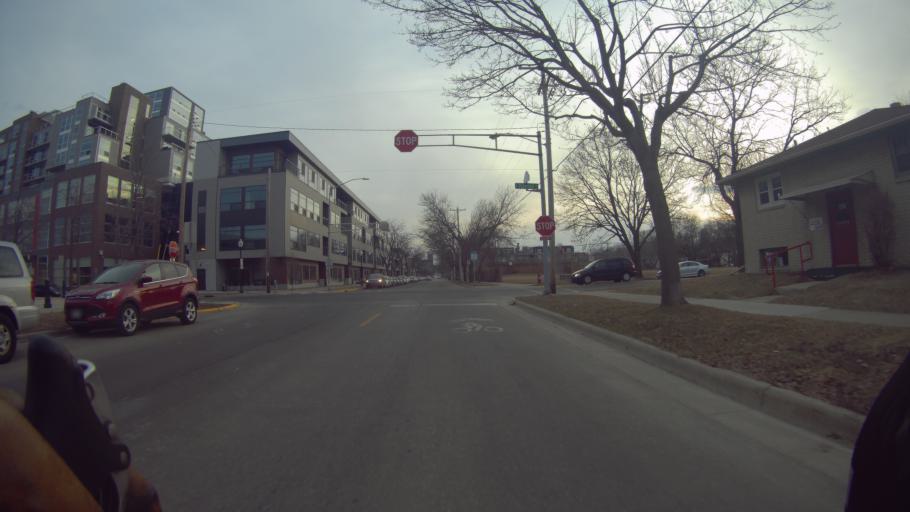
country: US
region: Wisconsin
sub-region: Dane County
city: Madison
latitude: 43.0833
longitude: -89.3743
